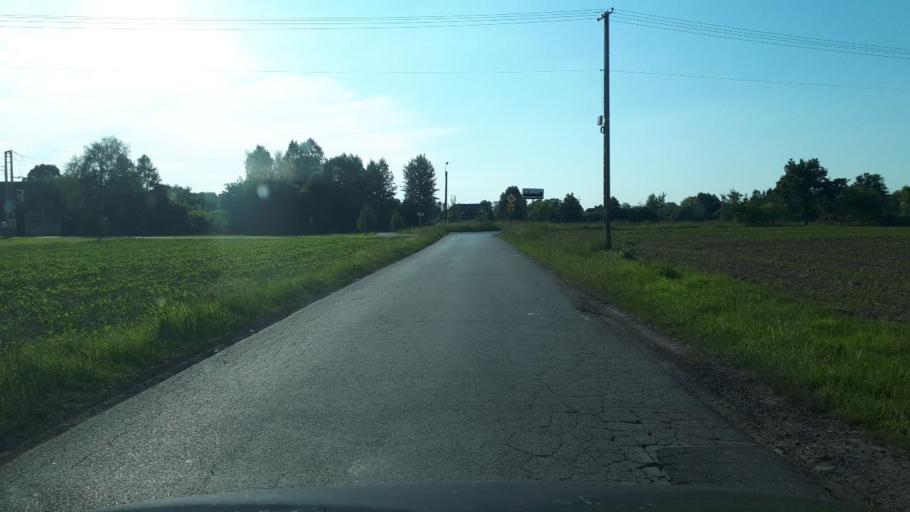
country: PL
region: Silesian Voivodeship
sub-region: Powiat bielski
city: Bronow
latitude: 49.8716
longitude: 18.9271
